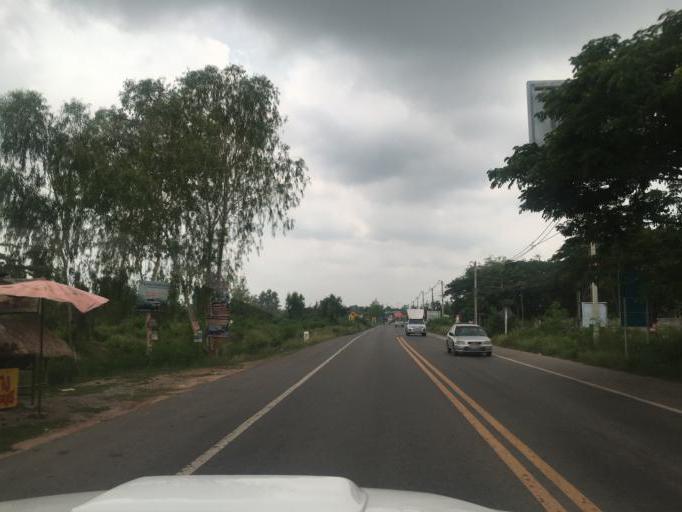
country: TH
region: Changwat Udon Thani
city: Udon Thani
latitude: 17.3693
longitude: 102.7217
